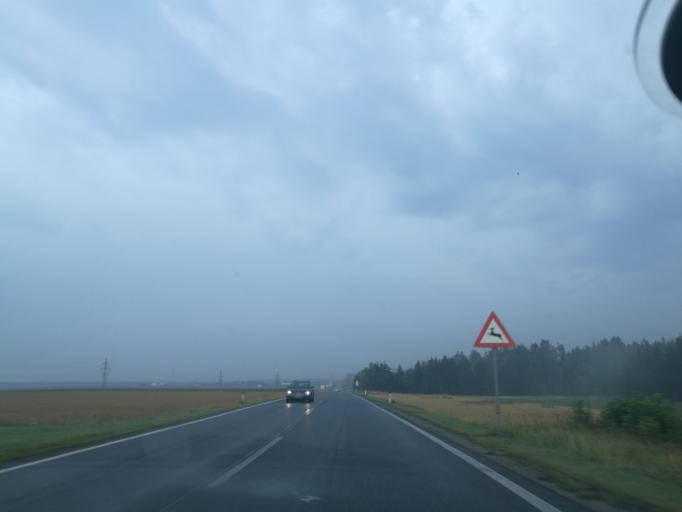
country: AT
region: Lower Austria
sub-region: Politischer Bezirk Zwettl
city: Gopfritz an der Wild
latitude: 48.7355
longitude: 15.3678
